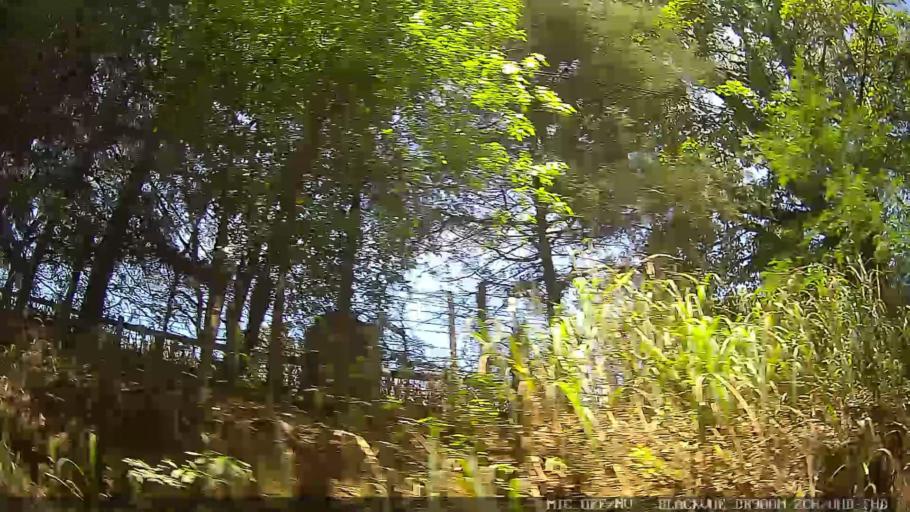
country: BR
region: Sao Paulo
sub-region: Jaguariuna
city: Jaguariuna
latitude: -22.7628
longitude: -47.0064
